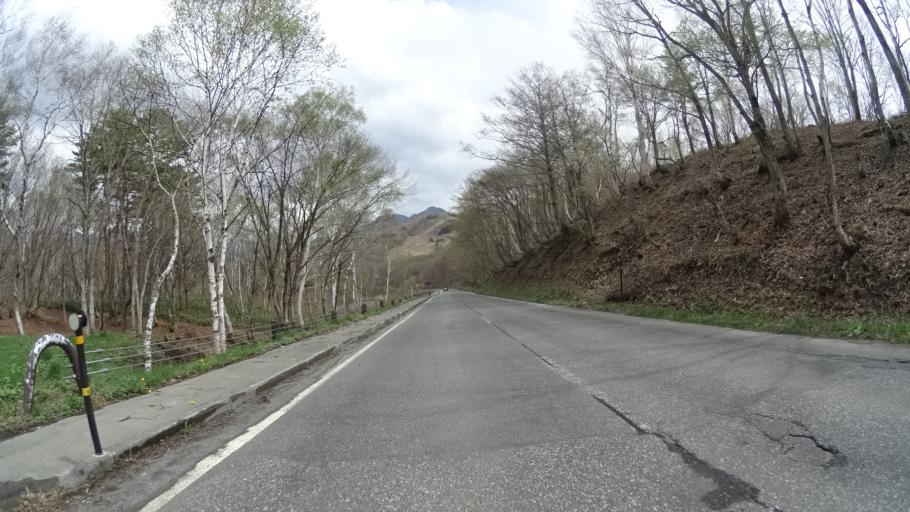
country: JP
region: Nagano
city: Nakano
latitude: 36.7200
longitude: 138.4778
